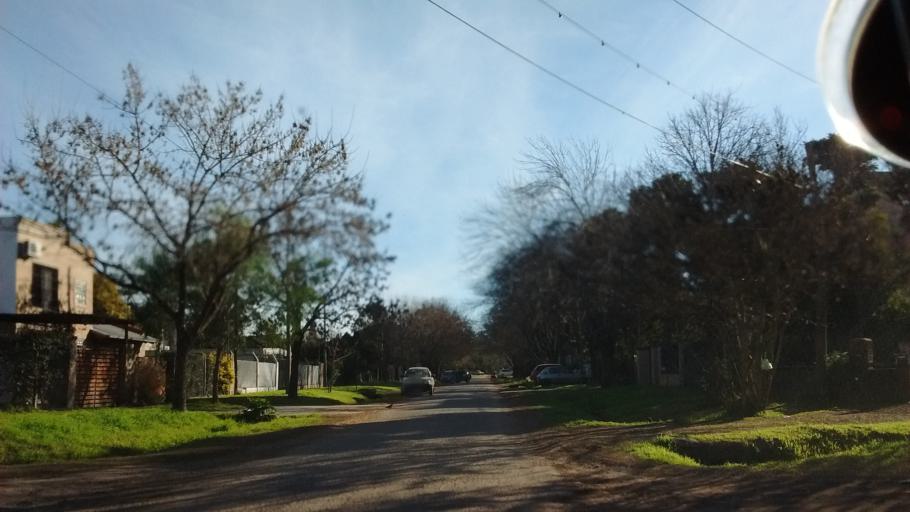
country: AR
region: Santa Fe
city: Funes
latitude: -32.9260
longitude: -60.8064
